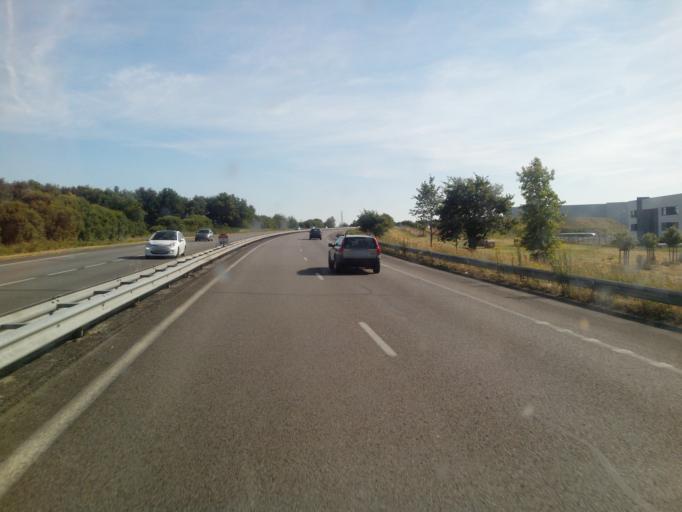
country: FR
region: Pays de la Loire
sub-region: Departement de la Loire-Atlantique
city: Heric
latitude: 47.3735
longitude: -1.6438
